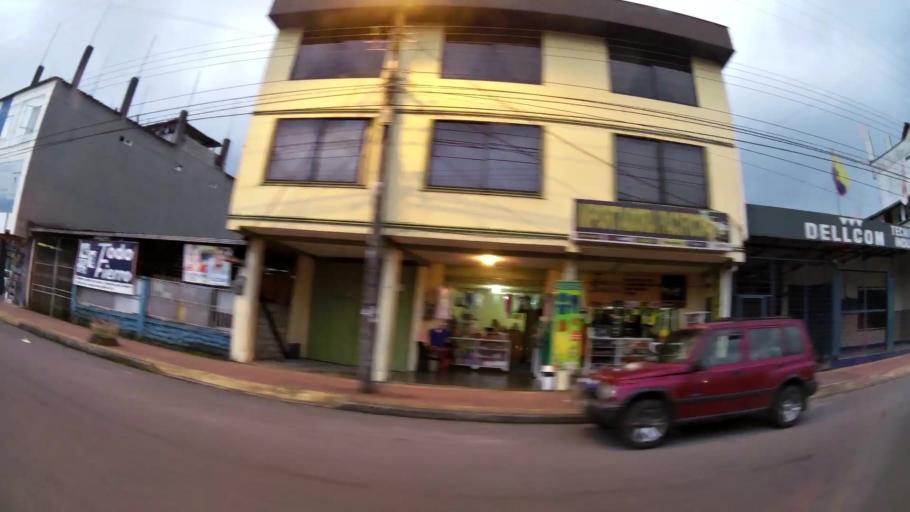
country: EC
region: Pastaza
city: Puyo
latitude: -1.4881
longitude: -78.0085
